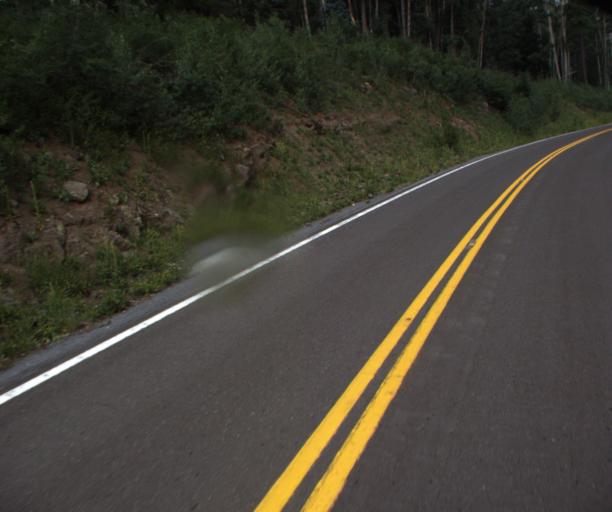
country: US
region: Arizona
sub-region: Greenlee County
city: Morenci
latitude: 33.5700
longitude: -109.3581
